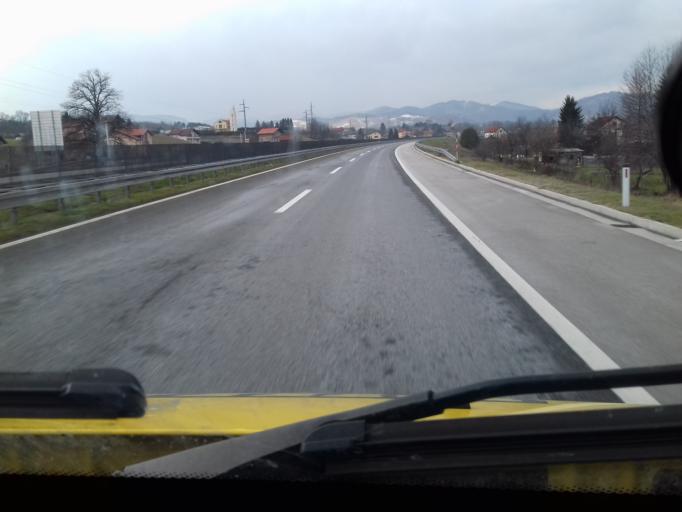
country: BA
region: Federation of Bosnia and Herzegovina
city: Gornje Mostre
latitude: 44.0104
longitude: 18.1430
